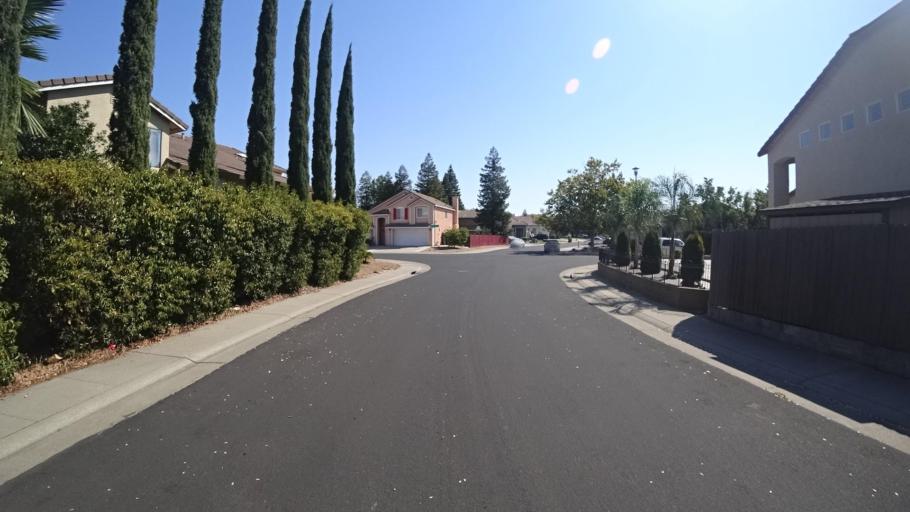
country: US
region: California
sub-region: Sacramento County
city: Vineyard
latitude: 38.4513
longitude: -121.3877
